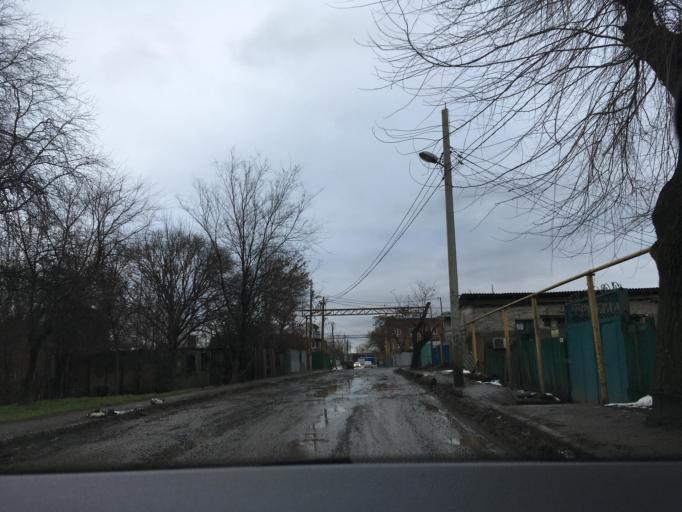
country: RU
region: Rostov
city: Rostov-na-Donu
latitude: 47.2107
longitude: 39.7177
